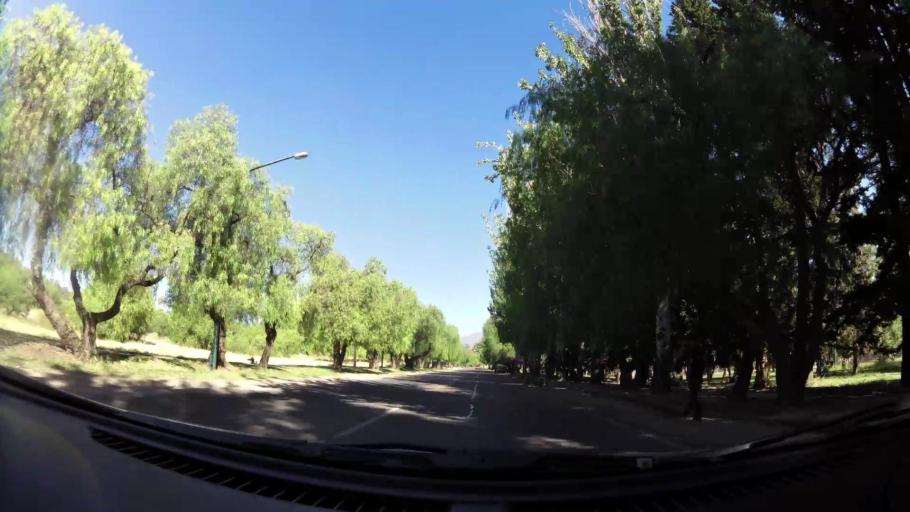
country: AR
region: Mendoza
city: Mendoza
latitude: -32.8927
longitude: -68.8785
